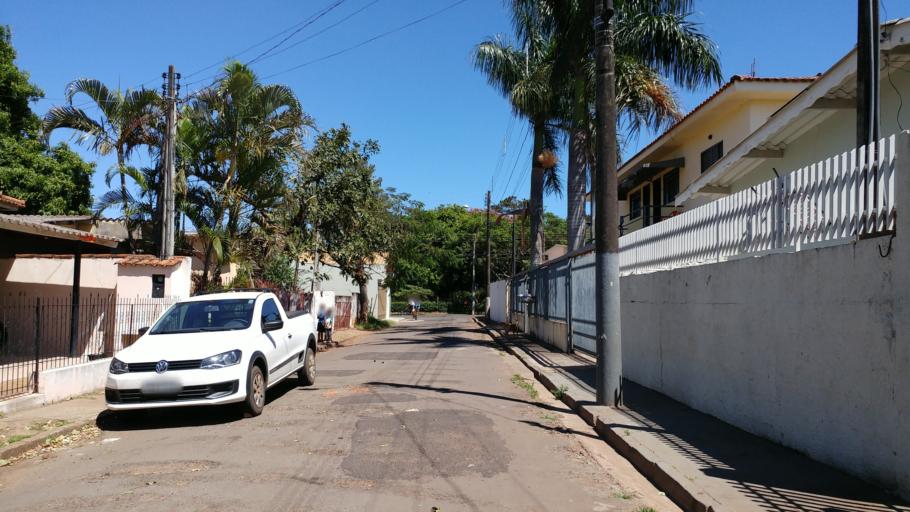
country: BR
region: Sao Paulo
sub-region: Paraguacu Paulista
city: Paraguacu Paulista
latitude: -22.4182
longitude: -50.5813
